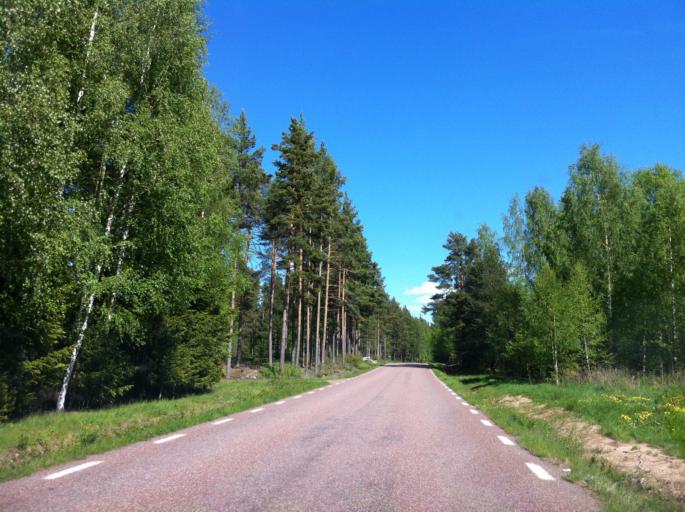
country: SE
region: Dalarna
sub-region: Mora Kommun
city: Mora
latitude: 60.9602
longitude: 14.6571
